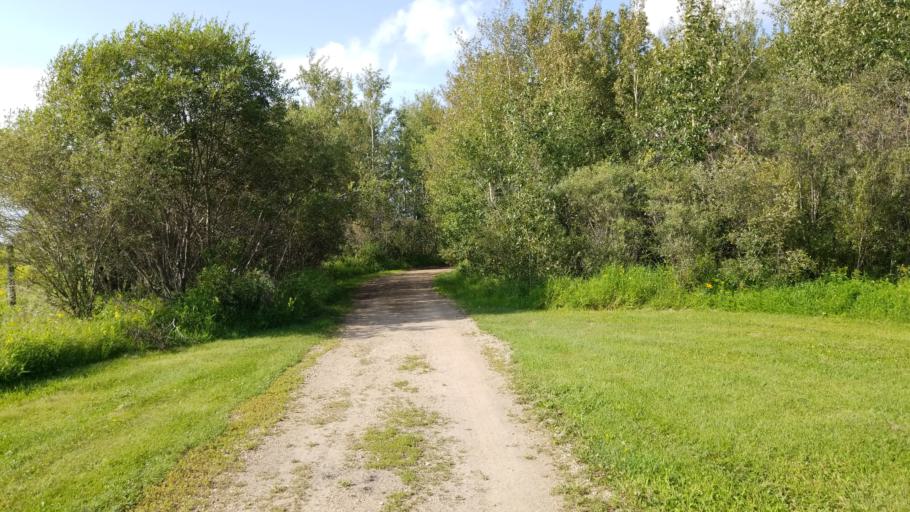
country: CA
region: Saskatchewan
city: Lloydminster
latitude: 53.2584
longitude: -110.0479
